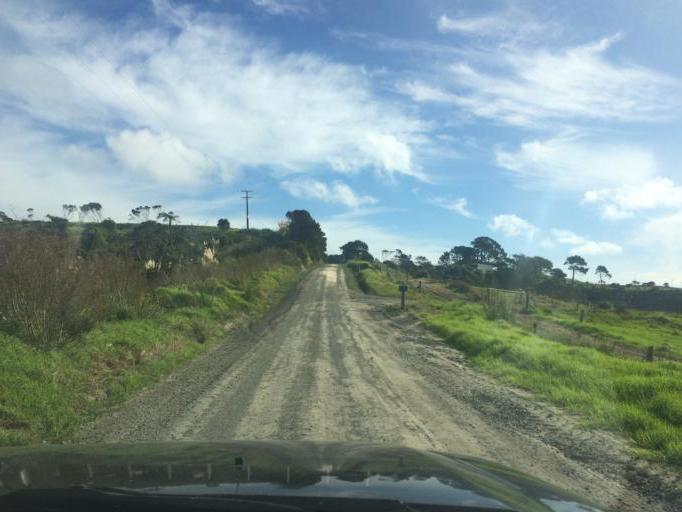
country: NZ
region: Northland
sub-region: Kaipara District
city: Dargaville
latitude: -36.0277
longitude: 173.8707
